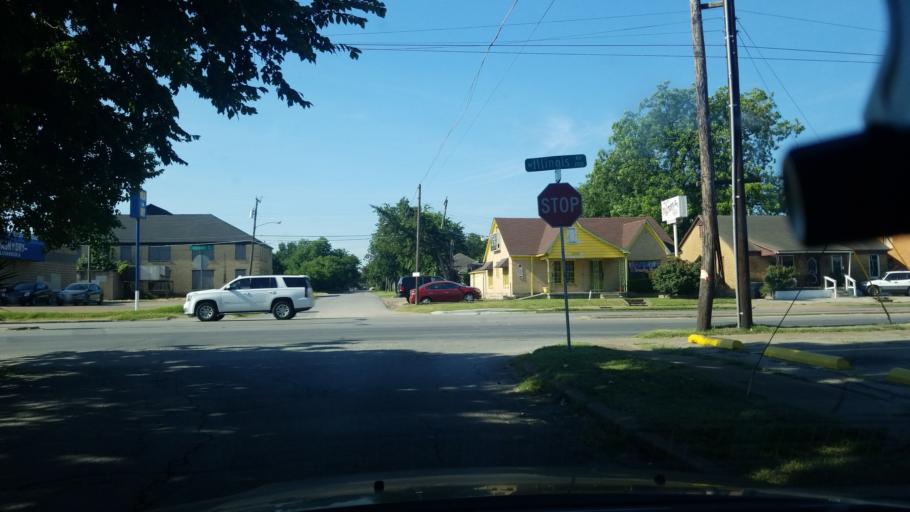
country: US
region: Texas
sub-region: Dallas County
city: Cockrell Hill
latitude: 32.7207
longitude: -96.8246
